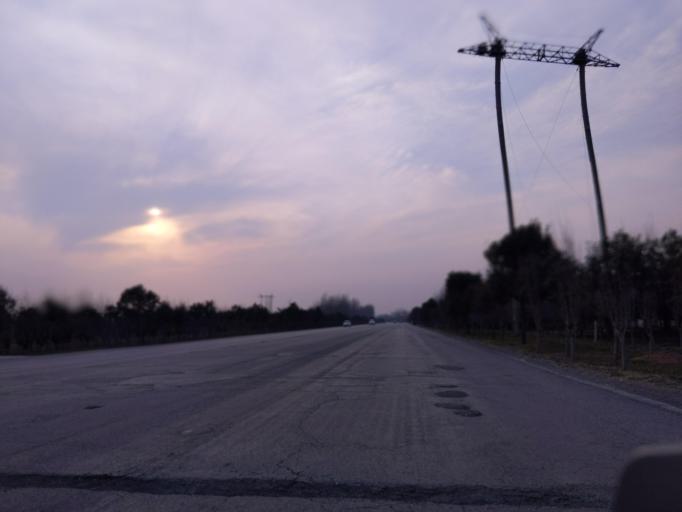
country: CN
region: Henan Sheng
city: Puyang
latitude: 35.8198
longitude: 114.9864
